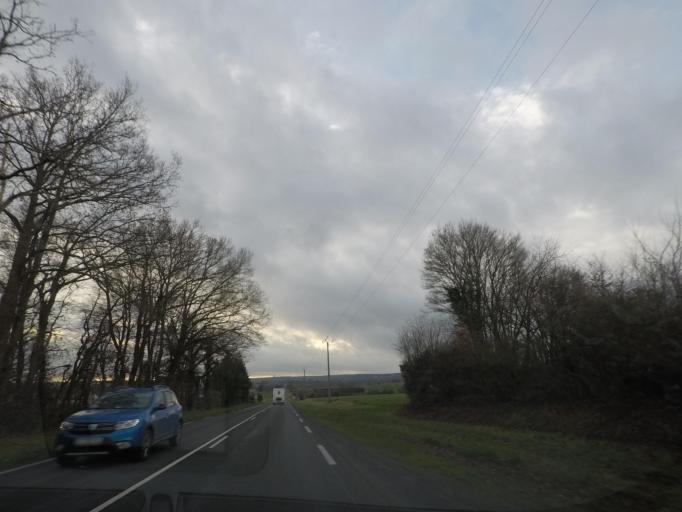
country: FR
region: Pays de la Loire
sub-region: Departement de la Sarthe
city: Vibraye
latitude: 48.0949
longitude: 0.7209
